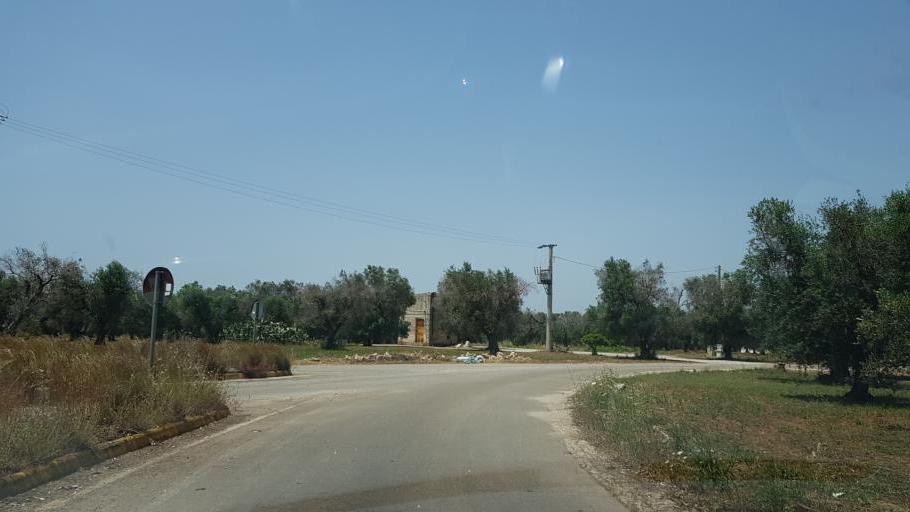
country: IT
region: Apulia
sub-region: Provincia di Lecce
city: Porto Cesareo
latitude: 40.3179
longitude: 17.8954
